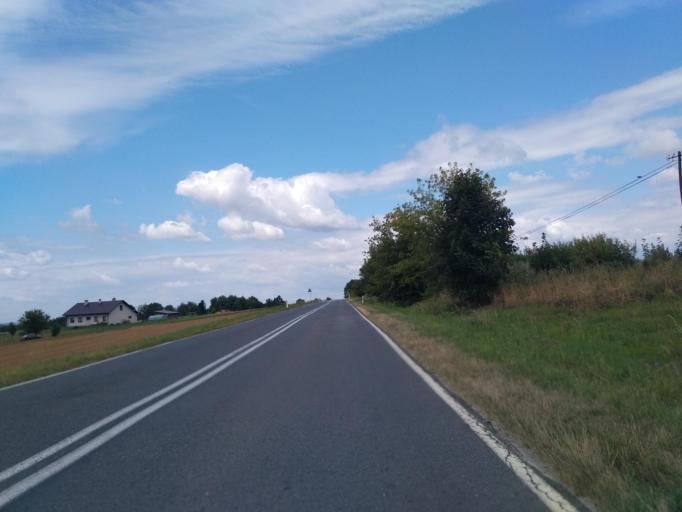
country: PL
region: Subcarpathian Voivodeship
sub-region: Powiat rzeszowski
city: Hyzne
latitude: 49.8940
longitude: 22.2307
